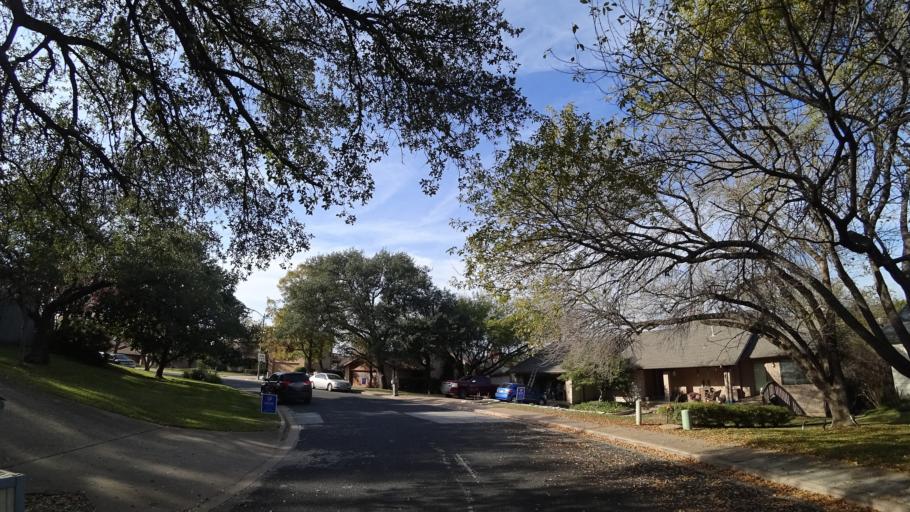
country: US
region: Texas
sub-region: Williamson County
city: Jollyville
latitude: 30.3864
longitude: -97.7563
